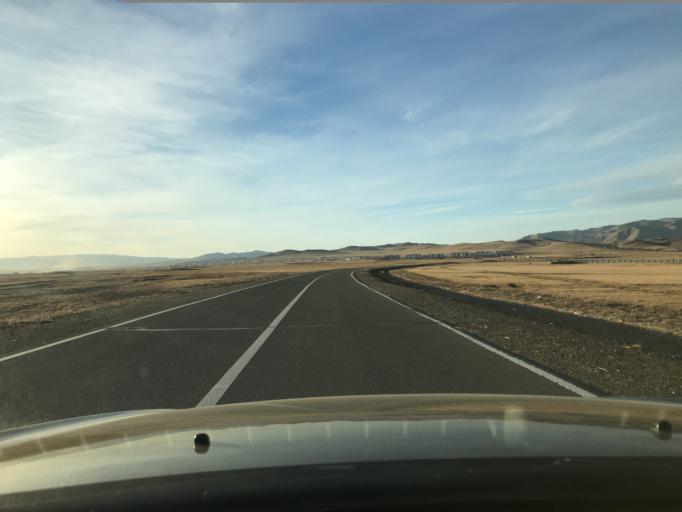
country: MN
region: Central Aimak
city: Arhust
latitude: 47.7680
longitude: 107.4192
